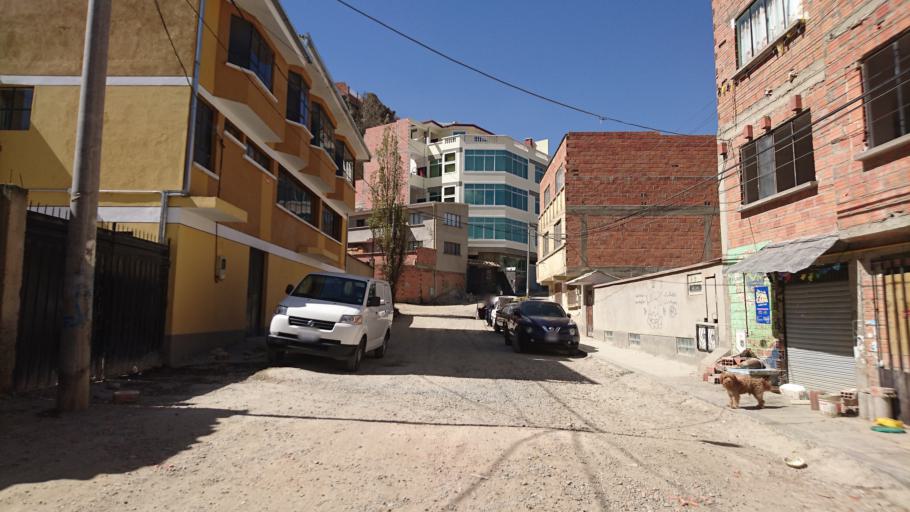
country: BO
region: La Paz
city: La Paz
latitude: -16.5262
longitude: -68.0982
